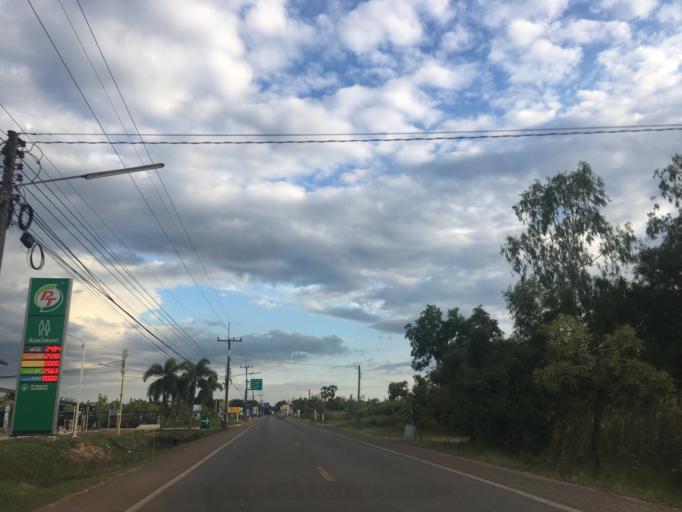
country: TH
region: Chanthaburi
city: Na Yai Am
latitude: 12.7097
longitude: 101.7752
